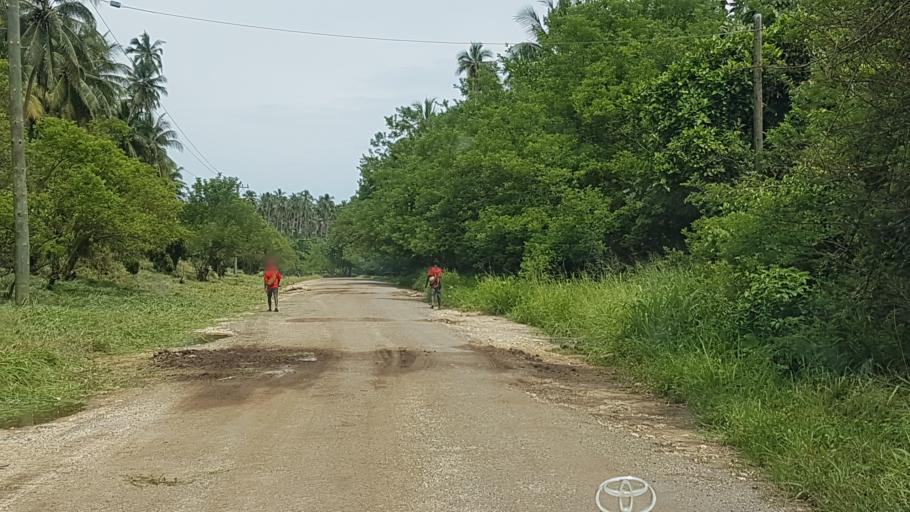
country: PG
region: Madang
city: Madang
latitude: -4.7849
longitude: 145.7145
